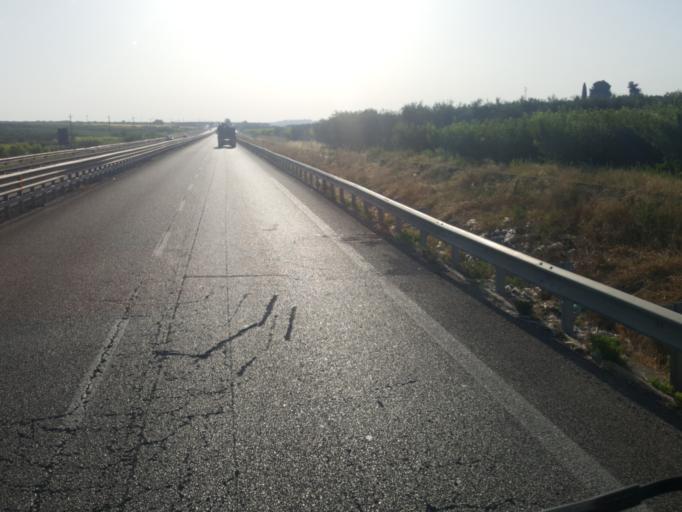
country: IT
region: Apulia
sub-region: Provincia di Barletta - Andria - Trani
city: San Ferdinando di Puglia
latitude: 41.2864
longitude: 16.0120
